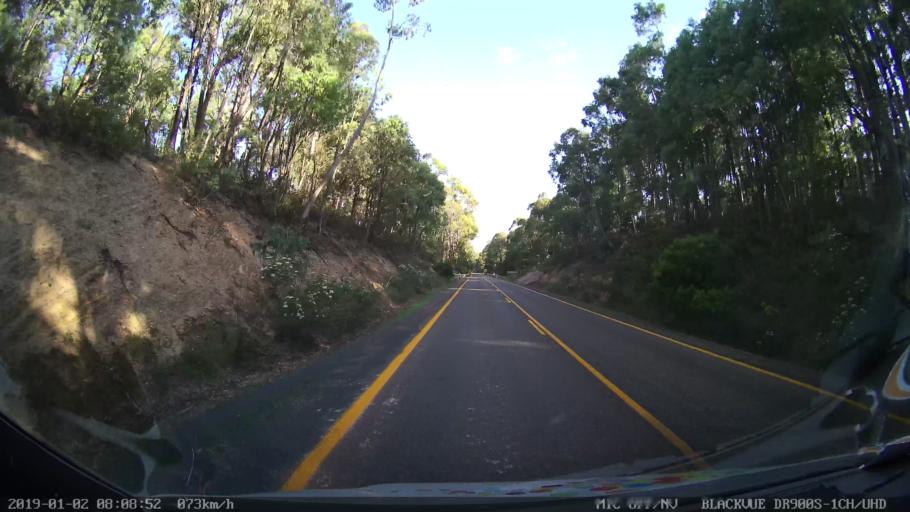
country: AU
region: New South Wales
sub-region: Tumut Shire
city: Tumut
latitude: -35.6126
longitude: 148.3820
